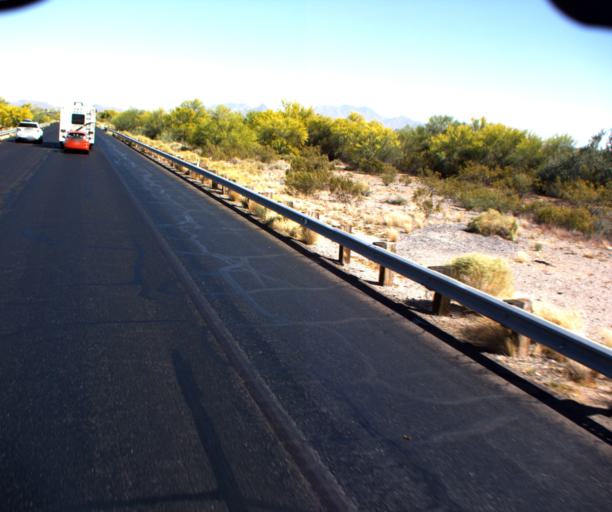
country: US
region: Arizona
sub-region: Pinal County
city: Maricopa
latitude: 32.8478
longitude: -112.3050
